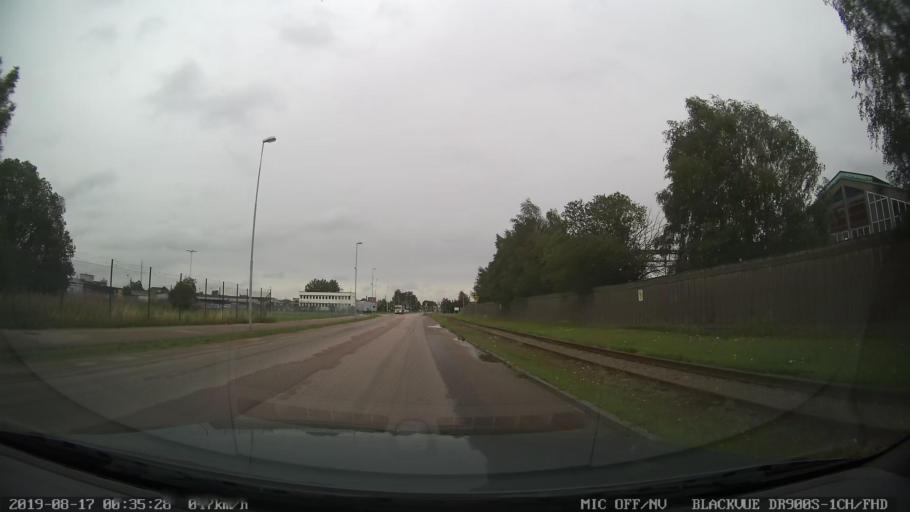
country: SE
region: Skane
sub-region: Landskrona
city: Landskrona
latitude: 55.8656
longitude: 12.8410
